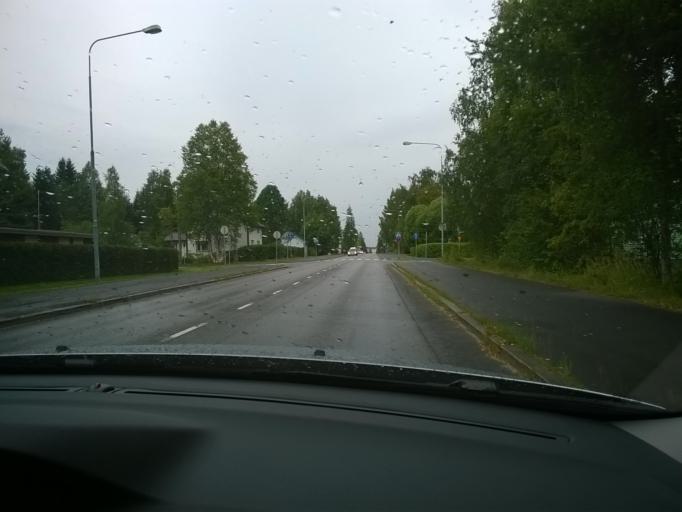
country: FI
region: Kainuu
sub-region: Kehys-Kainuu
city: Kuhmo
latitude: 64.1236
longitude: 29.5340
